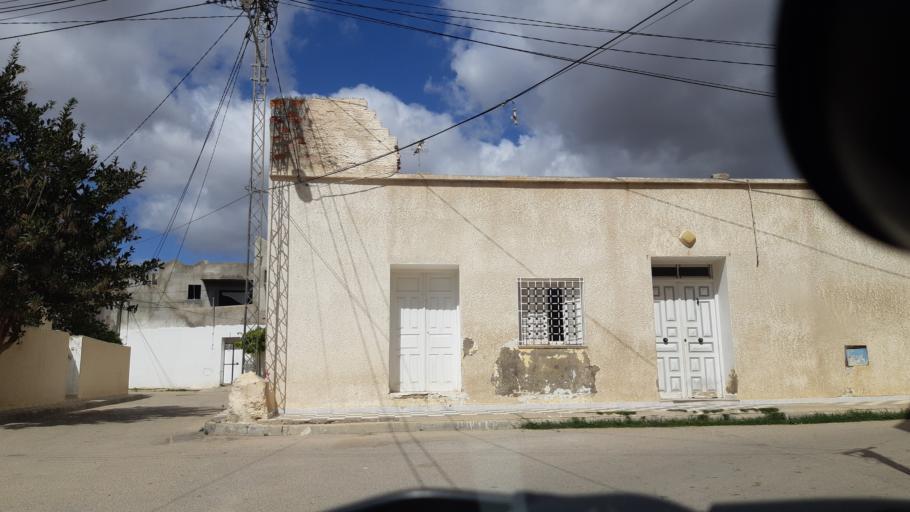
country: TN
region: Susah
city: Akouda
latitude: 35.8787
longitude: 10.5346
